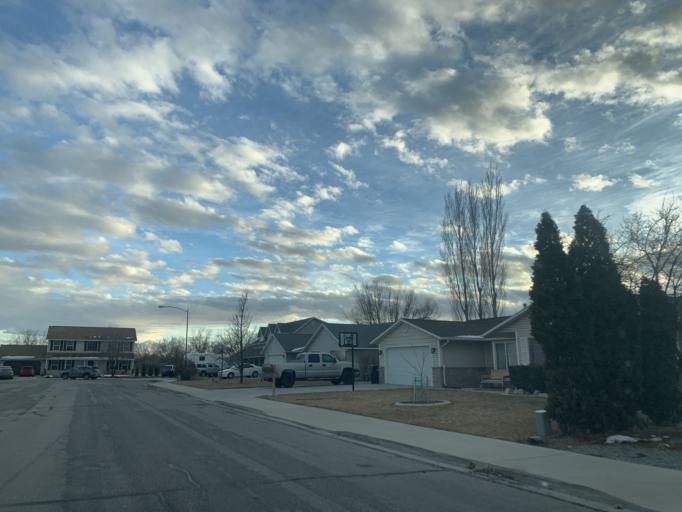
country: US
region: Utah
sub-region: Utah County
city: Orem
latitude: 40.2477
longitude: -111.7133
